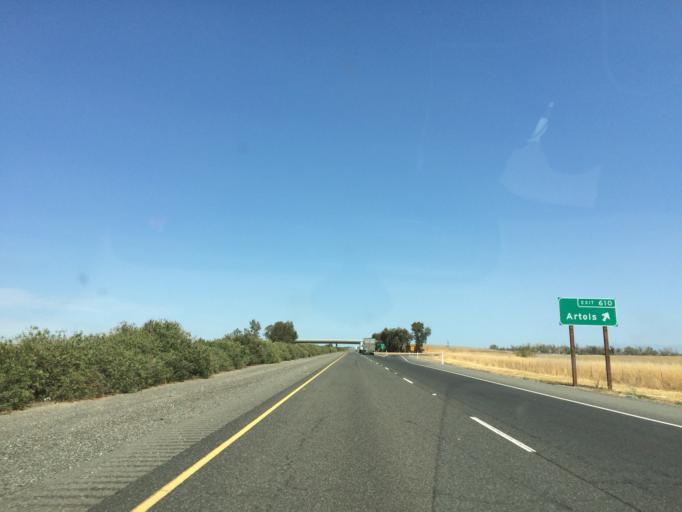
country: US
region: California
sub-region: Glenn County
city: Willows
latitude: 39.6203
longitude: -122.2057
